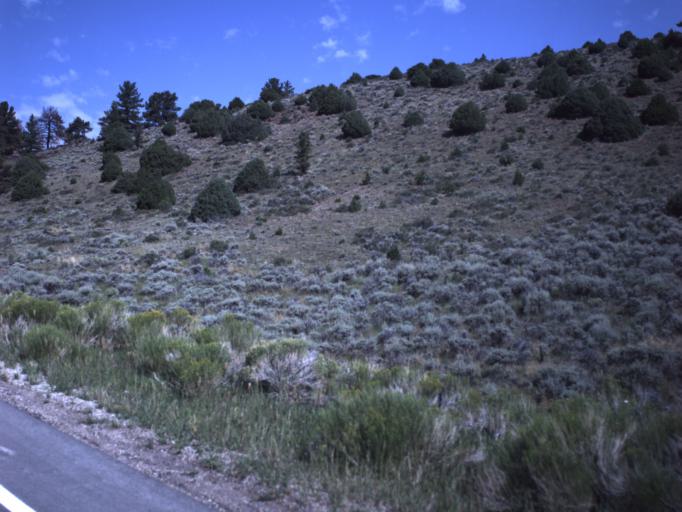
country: US
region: Utah
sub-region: Daggett County
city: Manila
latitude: 40.8835
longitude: -109.6966
